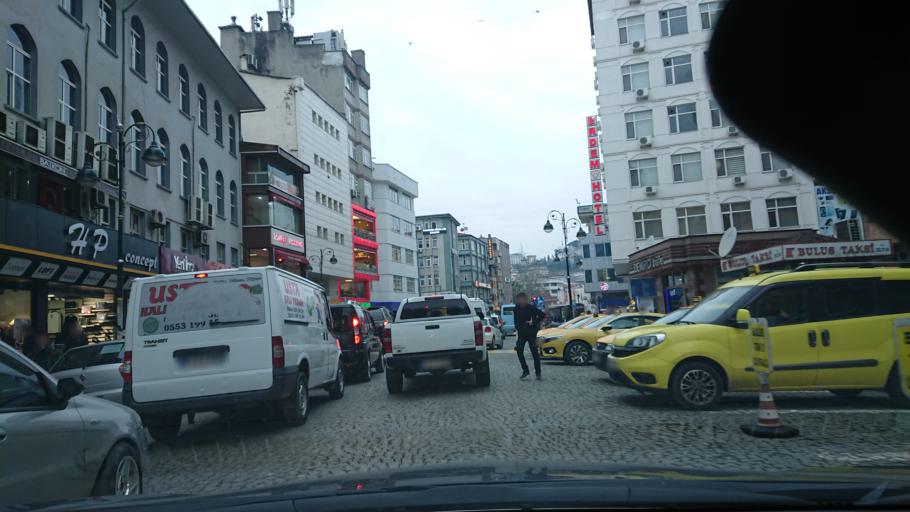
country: TR
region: Rize
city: Rize
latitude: 41.0247
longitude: 40.5209
